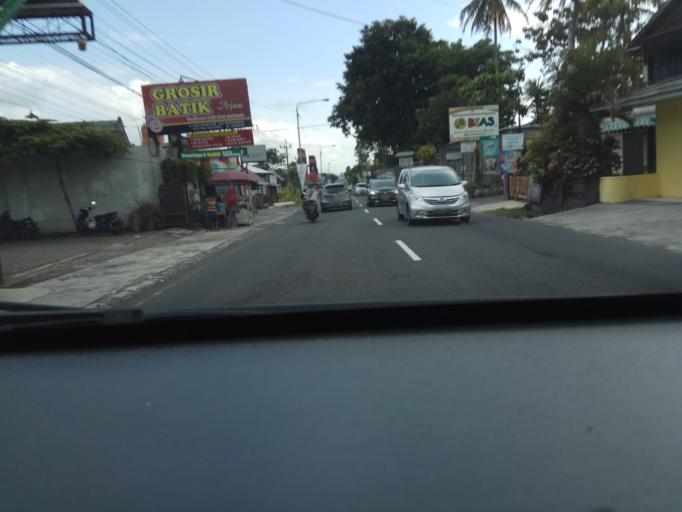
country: ID
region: Daerah Istimewa Yogyakarta
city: Melati
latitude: -7.7146
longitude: 110.4068
